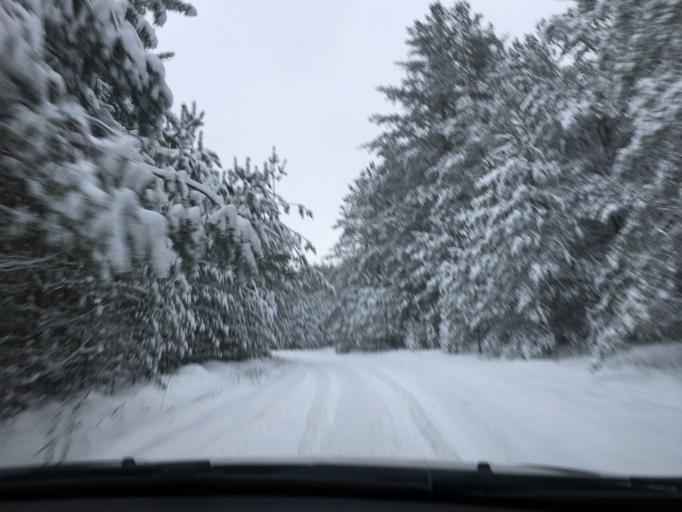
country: LT
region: Alytaus apskritis
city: Druskininkai
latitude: 53.9194
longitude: 24.1946
